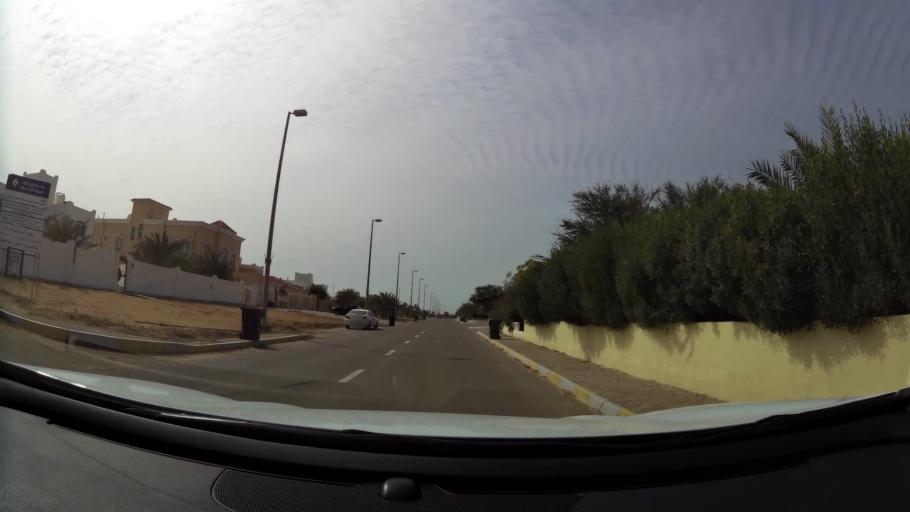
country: AE
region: Abu Dhabi
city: Abu Dhabi
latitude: 24.5706
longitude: 54.6901
